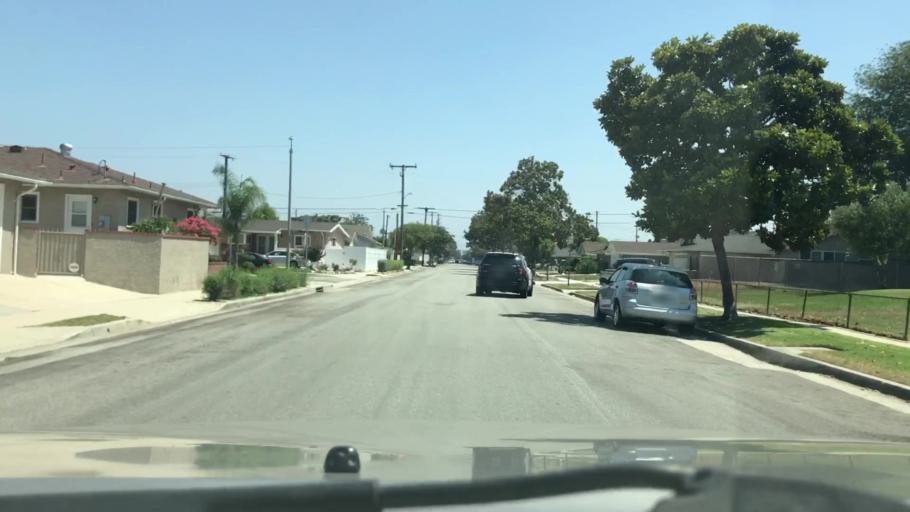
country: US
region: California
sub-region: Los Angeles County
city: Gardena
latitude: 33.8620
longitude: -118.3141
